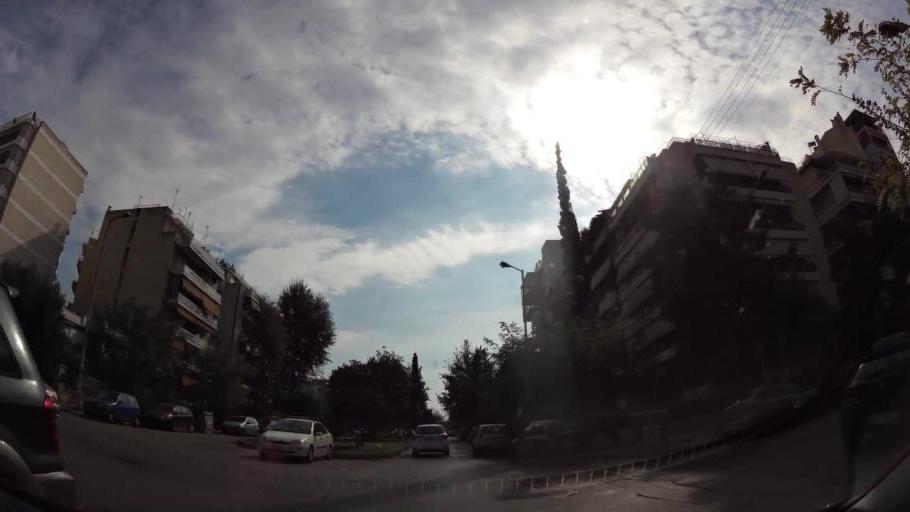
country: GR
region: Attica
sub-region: Nomarchia Athinas
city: Nea Smyrni
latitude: 37.9521
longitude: 23.7152
